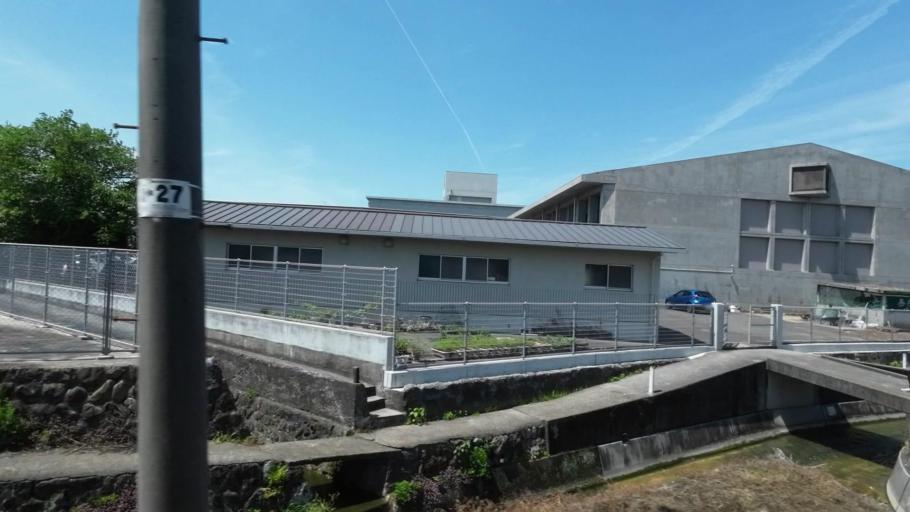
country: JP
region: Kagawa
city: Marugame
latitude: 34.2287
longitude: 133.7899
